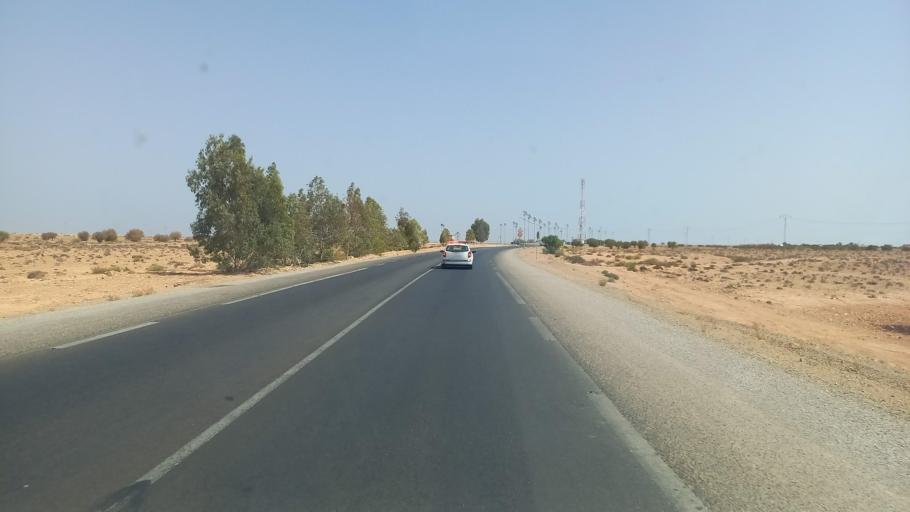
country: TN
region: Madanin
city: Medenine
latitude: 33.3831
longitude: 10.7002
